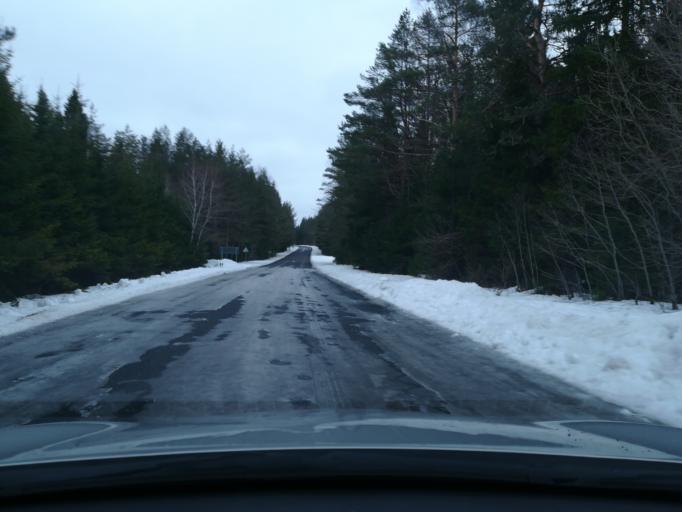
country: EE
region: Harju
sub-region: Nissi vald
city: Riisipere
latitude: 59.1102
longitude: 24.3245
